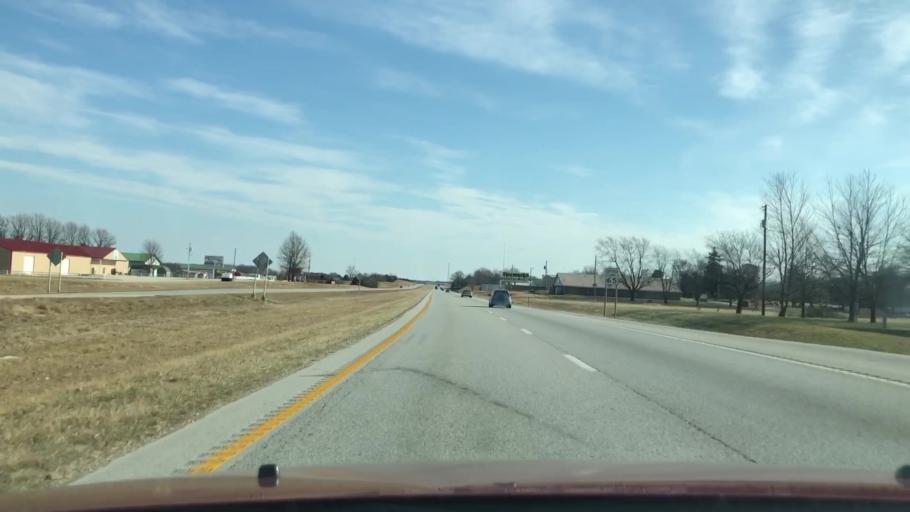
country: US
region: Missouri
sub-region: Webster County
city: Seymour
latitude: 37.1565
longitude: -92.7848
